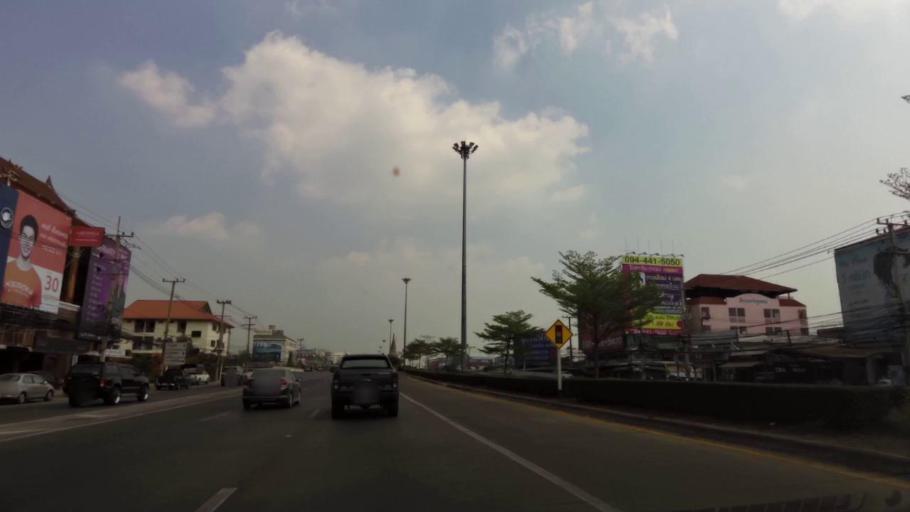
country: TH
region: Phra Nakhon Si Ayutthaya
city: Phra Nakhon Si Ayutthaya
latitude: 14.3534
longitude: 100.5891
